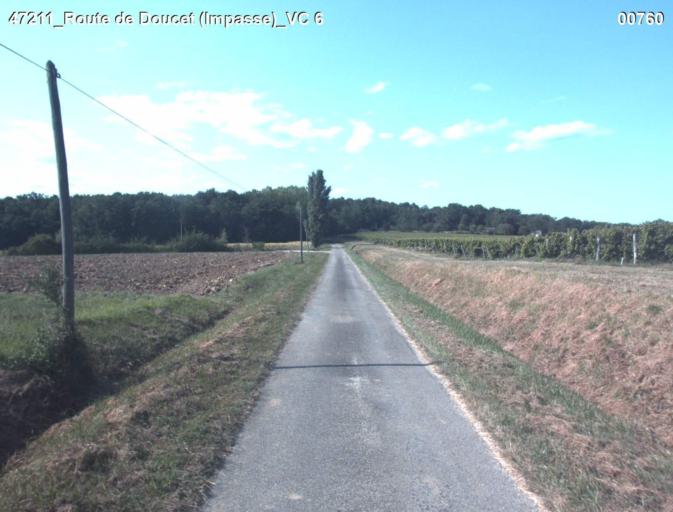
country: FR
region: Midi-Pyrenees
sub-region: Departement du Gers
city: Montreal
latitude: 44.0161
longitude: 0.2019
